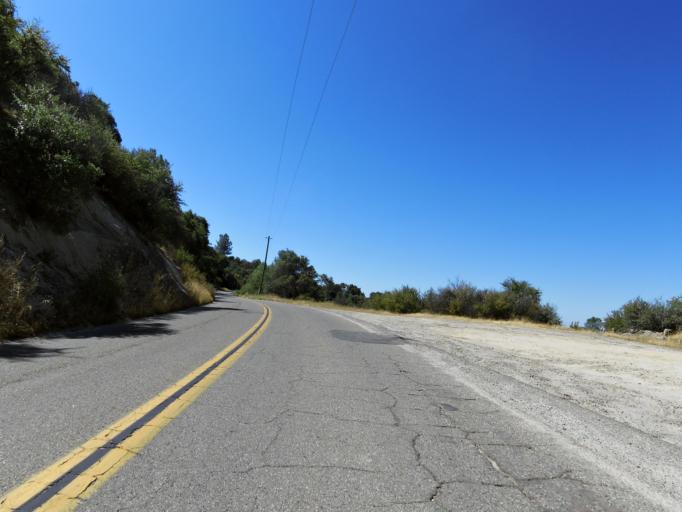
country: US
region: California
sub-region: Fresno County
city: Auberry
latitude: 37.2135
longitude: -119.4805
